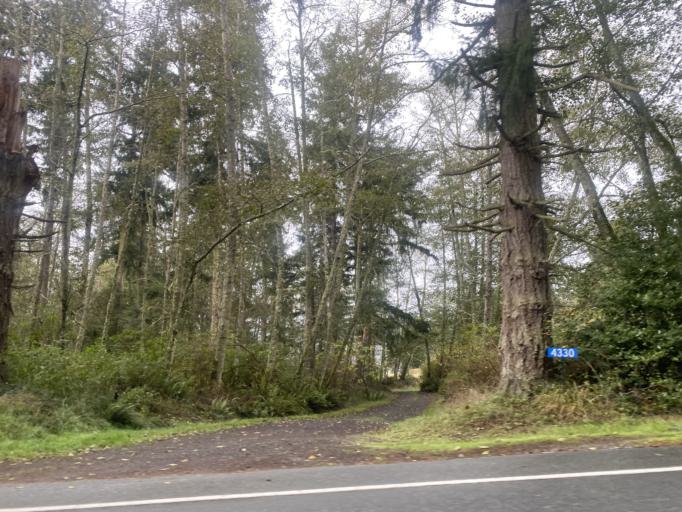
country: US
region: Washington
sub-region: Island County
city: Freeland
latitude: 48.0539
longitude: -122.5067
